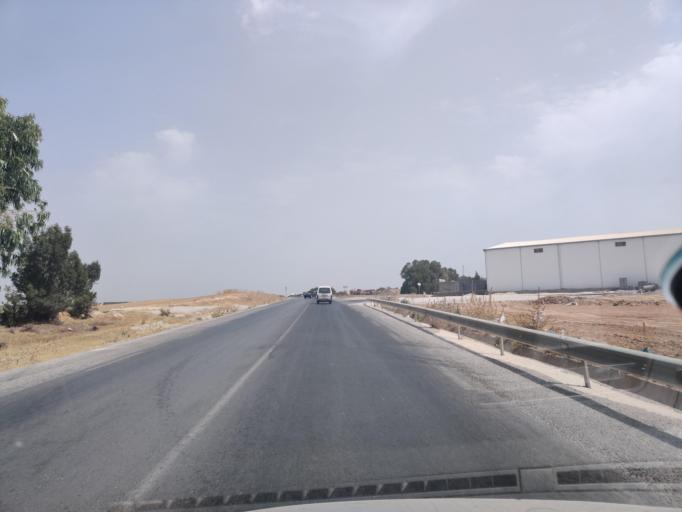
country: TN
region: Nabul
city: Bu `Urqub
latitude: 36.4649
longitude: 10.5716
